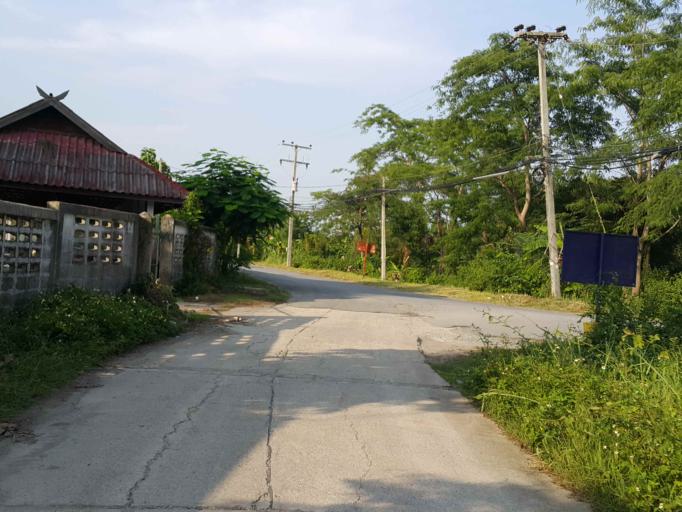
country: TH
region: Chiang Mai
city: San Sai
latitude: 18.8452
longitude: 99.0973
